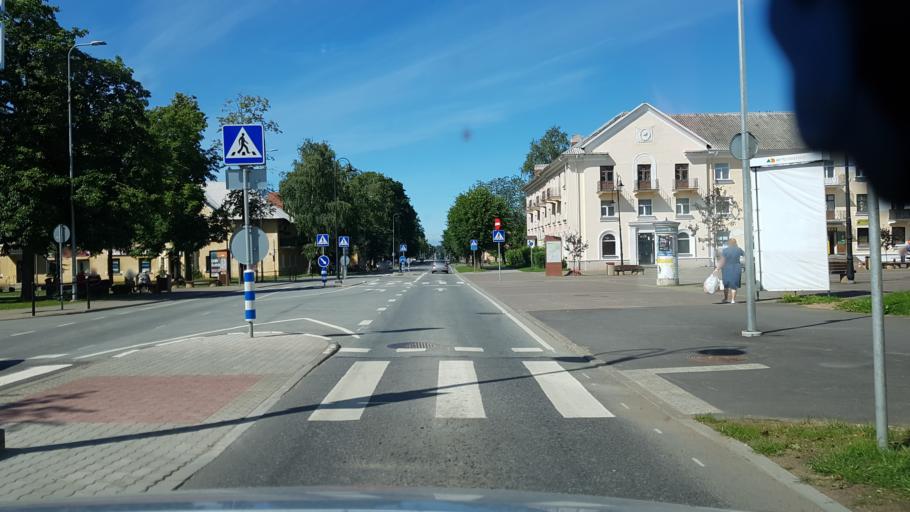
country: EE
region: Ida-Virumaa
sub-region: Kohtla-Jaerve linn
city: Kohtla-Jarve
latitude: 59.4019
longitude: 27.2877
